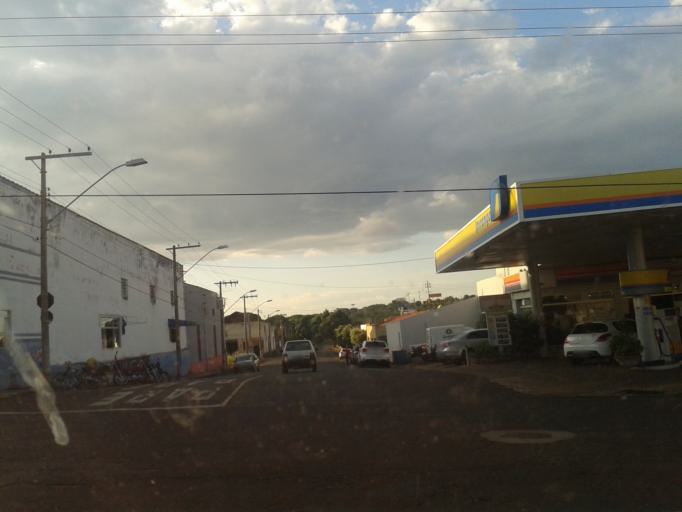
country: BR
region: Minas Gerais
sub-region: Ituiutaba
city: Ituiutaba
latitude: -18.9687
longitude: -49.4606
